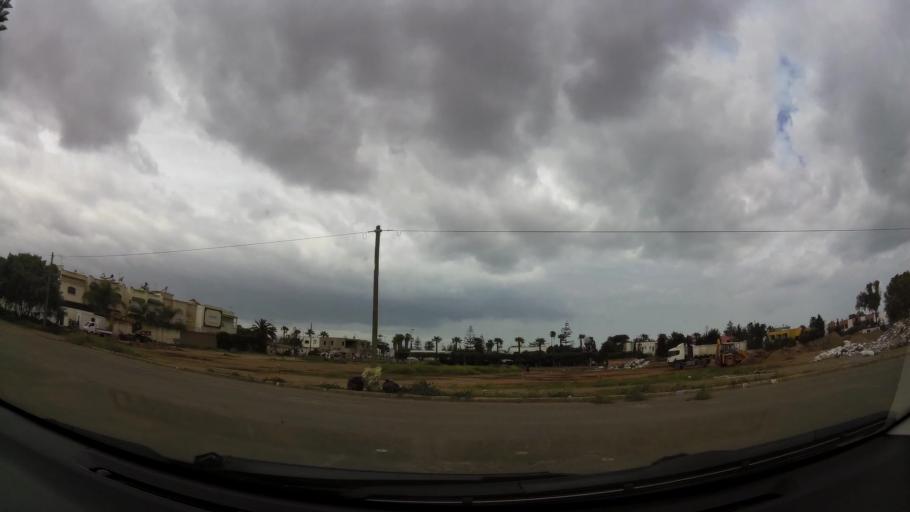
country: MA
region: Grand Casablanca
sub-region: Casablanca
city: Casablanca
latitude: 33.5803
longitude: -7.6510
